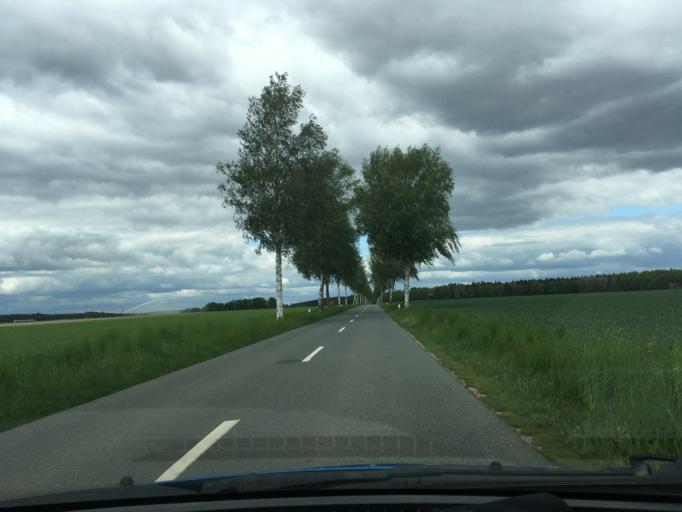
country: DE
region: Lower Saxony
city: Gerdau
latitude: 52.9235
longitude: 10.4135
